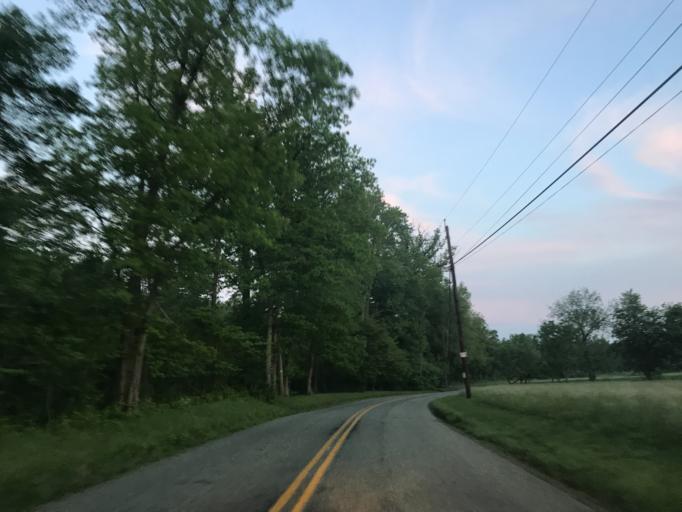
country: US
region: Maryland
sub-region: Harford County
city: Joppatowne
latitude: 39.4604
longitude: -76.3251
